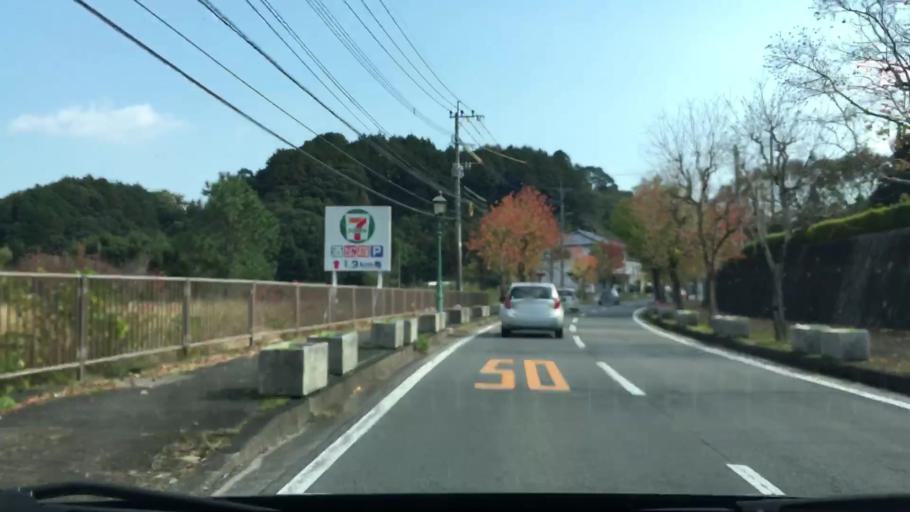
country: JP
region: Nagasaki
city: Sasebo
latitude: 32.9912
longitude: 129.7637
